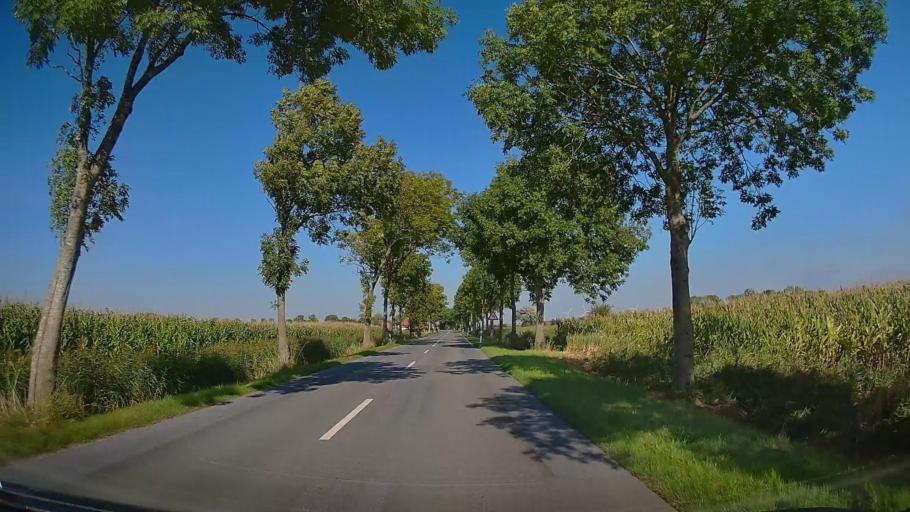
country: DE
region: Lower Saxony
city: Wremen
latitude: 53.6206
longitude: 8.5302
